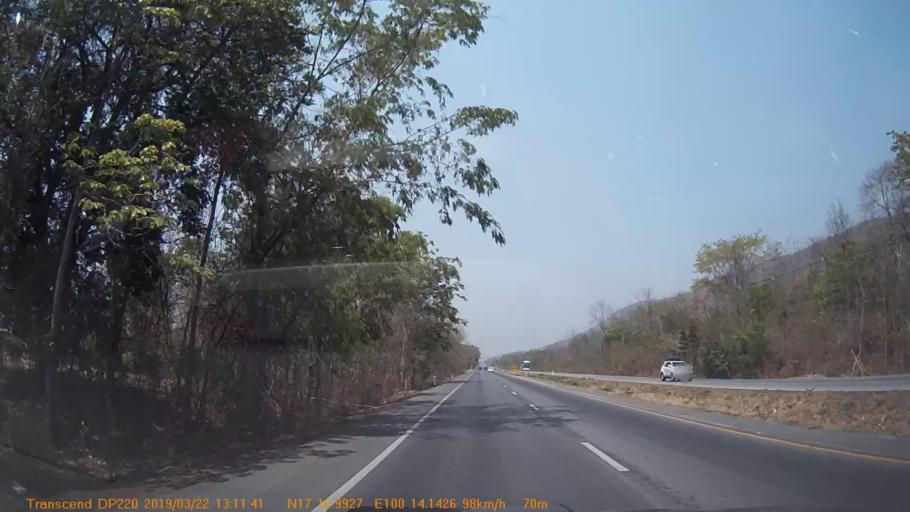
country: TH
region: Uttaradit
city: Phichai
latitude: 17.2836
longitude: 100.2356
